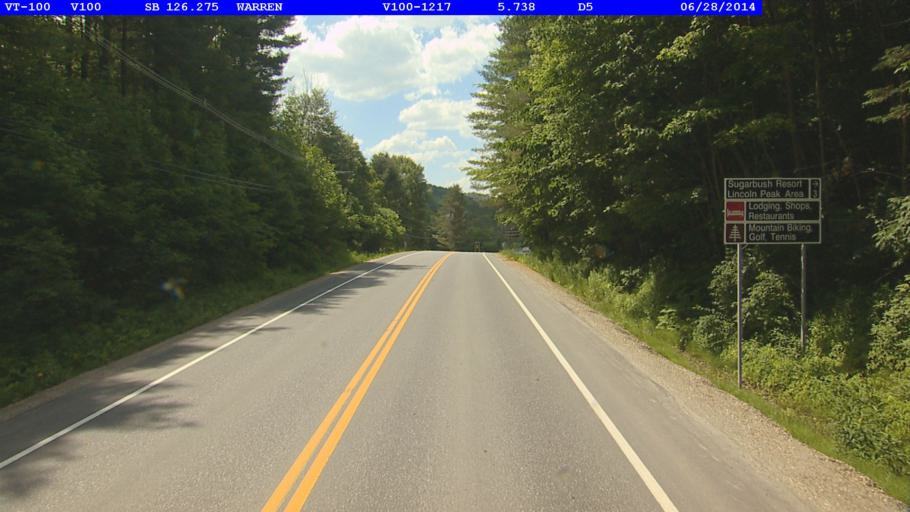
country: US
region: Vermont
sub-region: Washington County
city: Northfield
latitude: 44.1390
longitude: -72.8458
